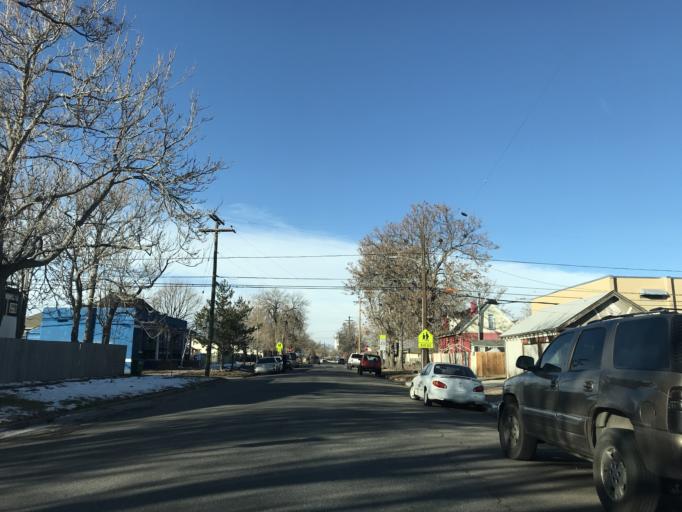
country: US
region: Colorado
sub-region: Denver County
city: Denver
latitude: 39.7658
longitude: -104.9696
